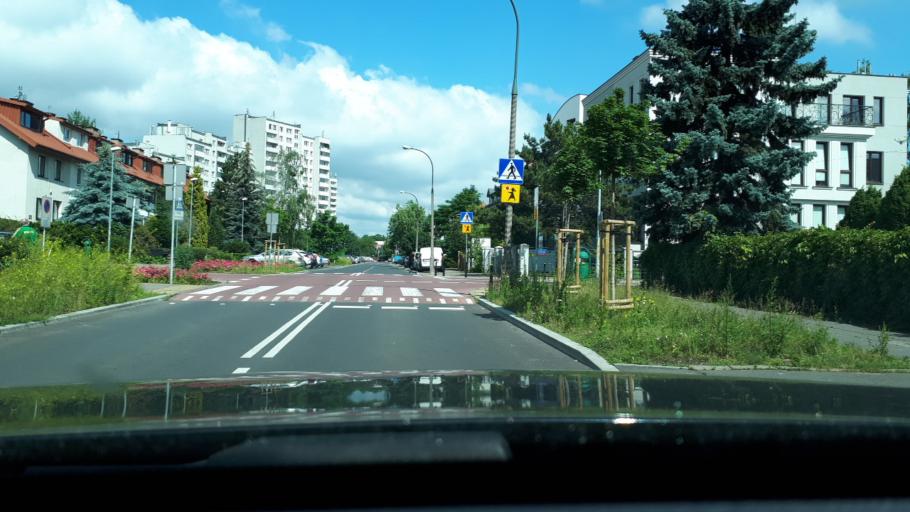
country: PL
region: Masovian Voivodeship
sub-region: Warszawa
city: Wilanow
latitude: 52.1738
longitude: 21.0722
